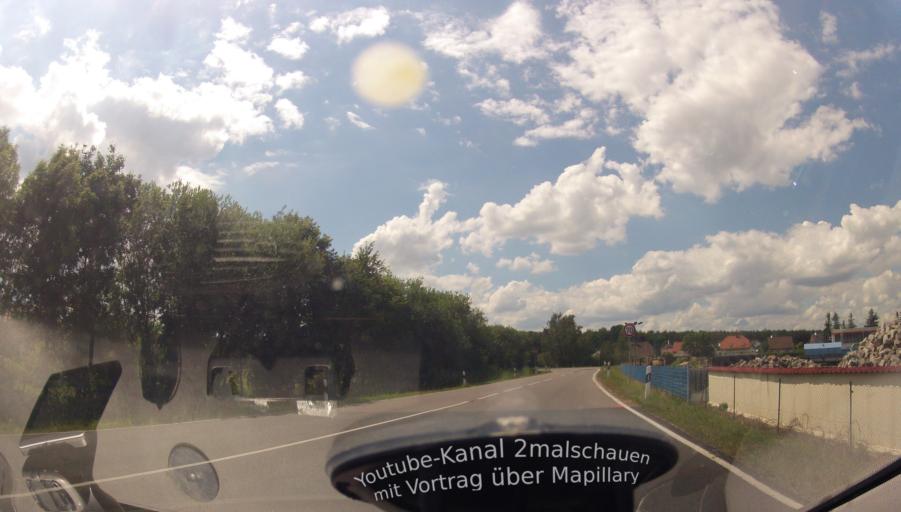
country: DE
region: Saxony
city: Torgau
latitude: 51.5279
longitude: 12.9949
